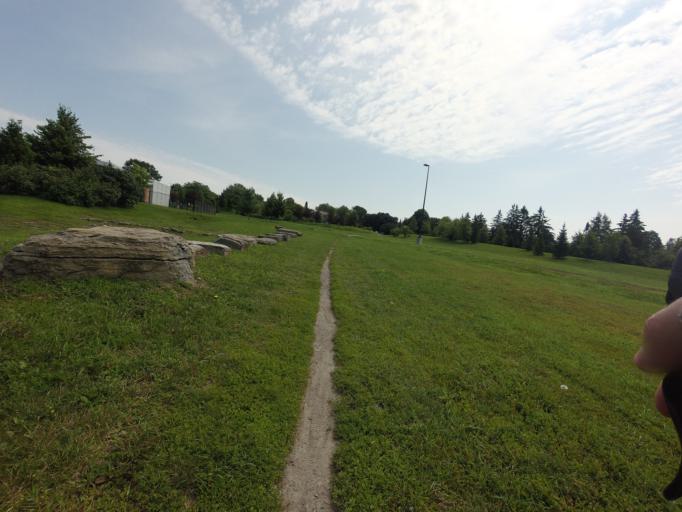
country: CA
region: Ontario
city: Ottawa
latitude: 45.3510
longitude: -75.7503
